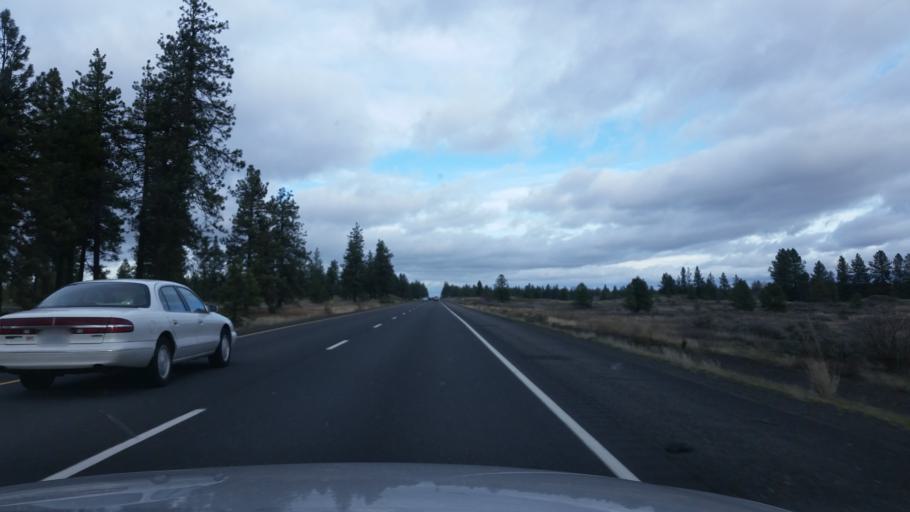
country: US
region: Washington
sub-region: Spokane County
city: Medical Lake
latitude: 47.4134
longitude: -117.8181
